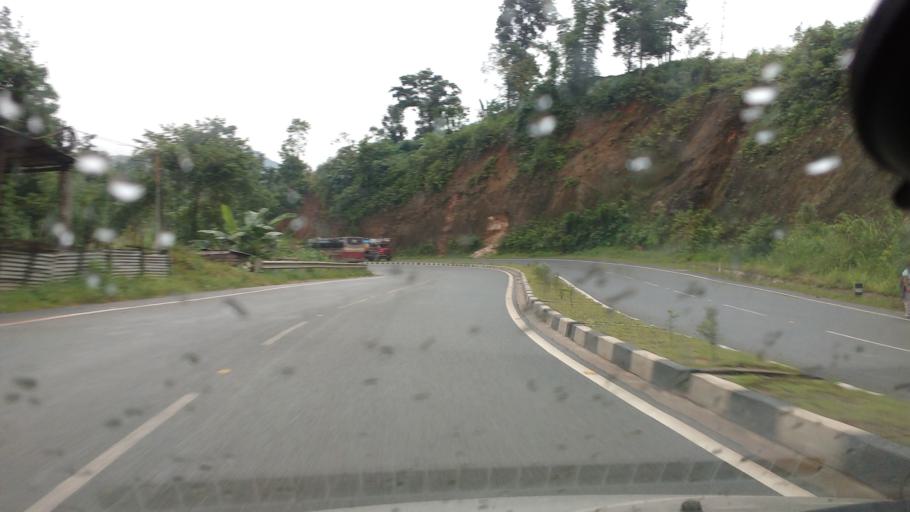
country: IN
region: Meghalaya
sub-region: Ri-Bhoi
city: Nongpoh
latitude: 25.8220
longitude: 91.8705
